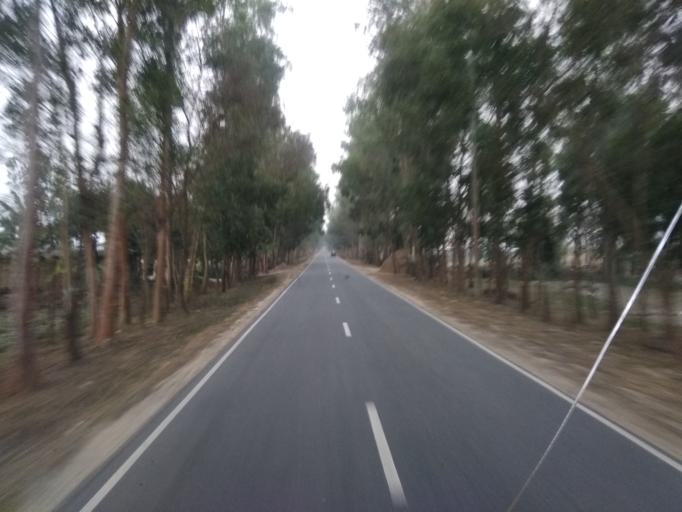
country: BD
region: Rajshahi
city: Bogra
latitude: 24.6603
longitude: 89.2673
